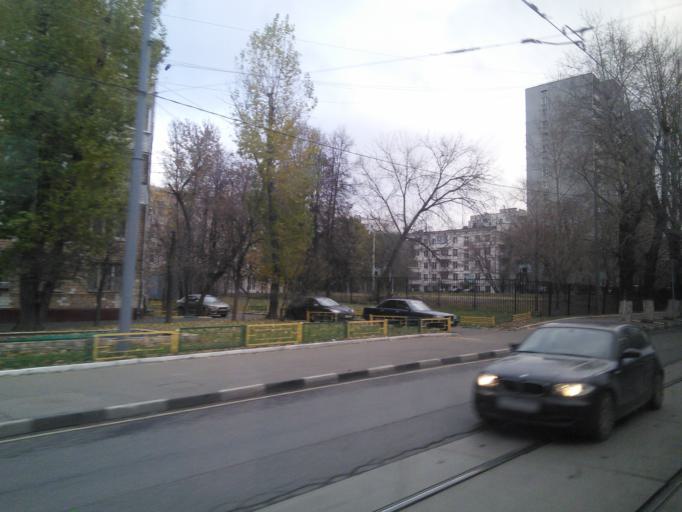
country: RU
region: Moscow
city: Lefortovo
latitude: 55.7625
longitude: 37.7096
